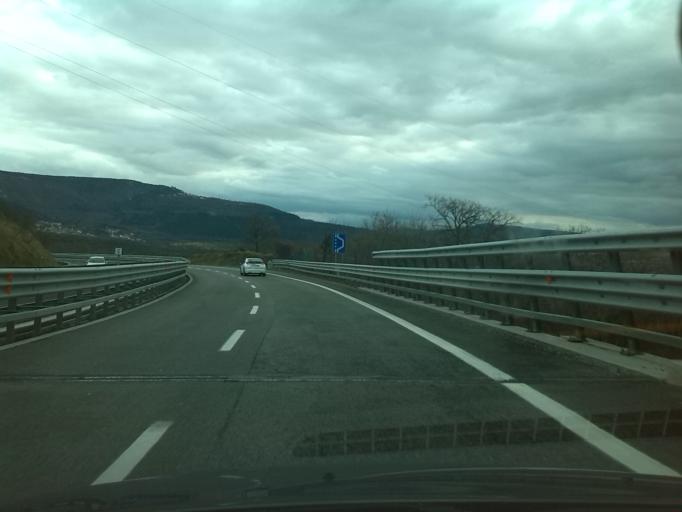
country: IT
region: Friuli Venezia Giulia
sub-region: Provincia di Trieste
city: Domio
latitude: 45.6267
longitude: 13.8311
